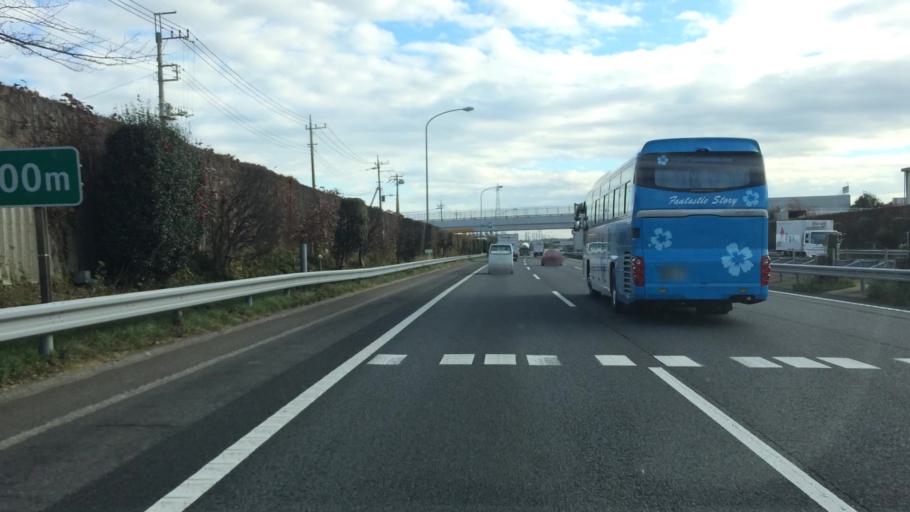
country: JP
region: Chiba
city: Yotsukaido
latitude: 35.6819
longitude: 140.1488
